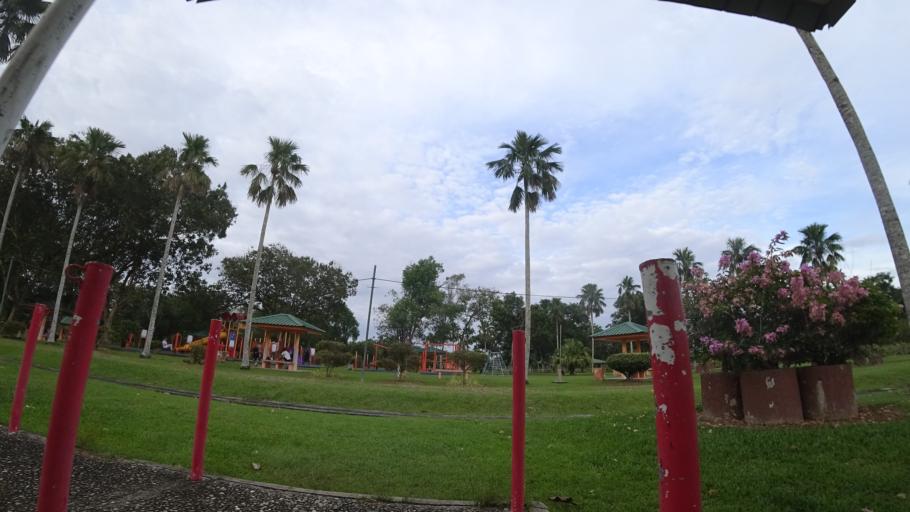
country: BN
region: Brunei and Muara
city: Bandar Seri Begawan
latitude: 4.8072
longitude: 114.8320
